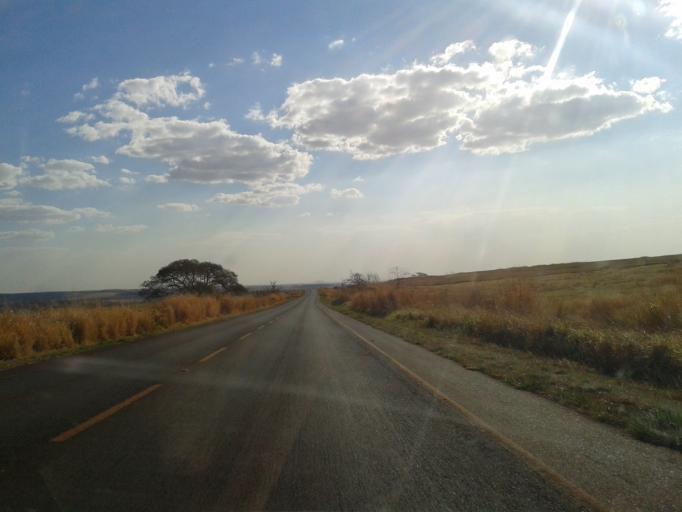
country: BR
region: Minas Gerais
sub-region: Centralina
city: Centralina
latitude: -18.7326
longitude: -49.2416
